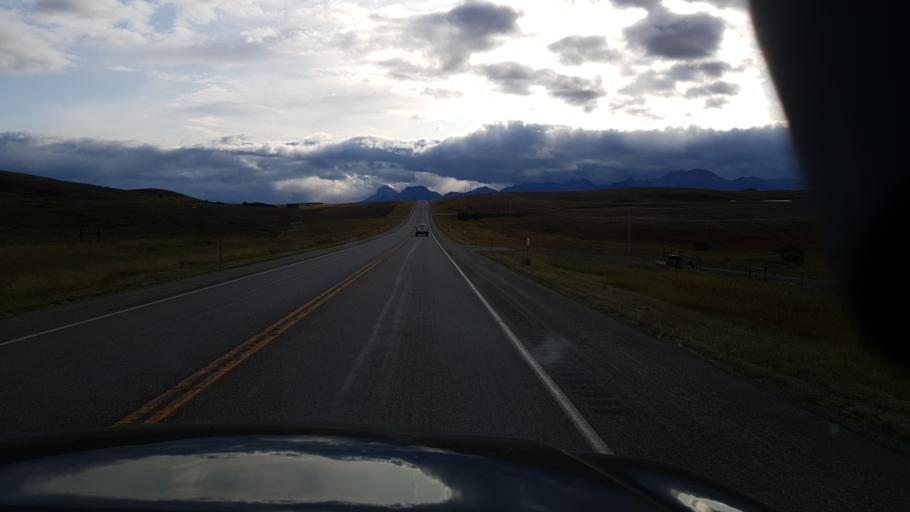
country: US
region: Montana
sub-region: Glacier County
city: South Browning
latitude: 48.5049
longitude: -113.1059
